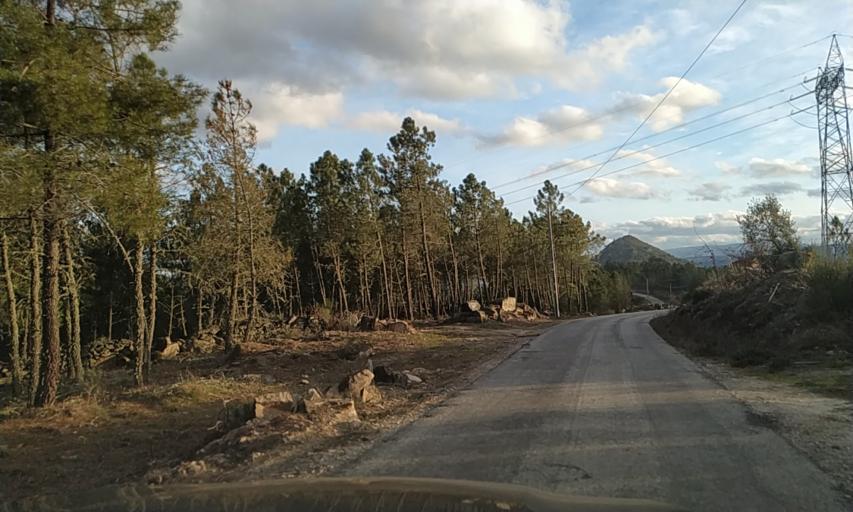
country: PT
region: Braganca
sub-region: Carrazeda de Ansiaes
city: Carrazeda de Anciaes
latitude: 41.2169
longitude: -7.3628
